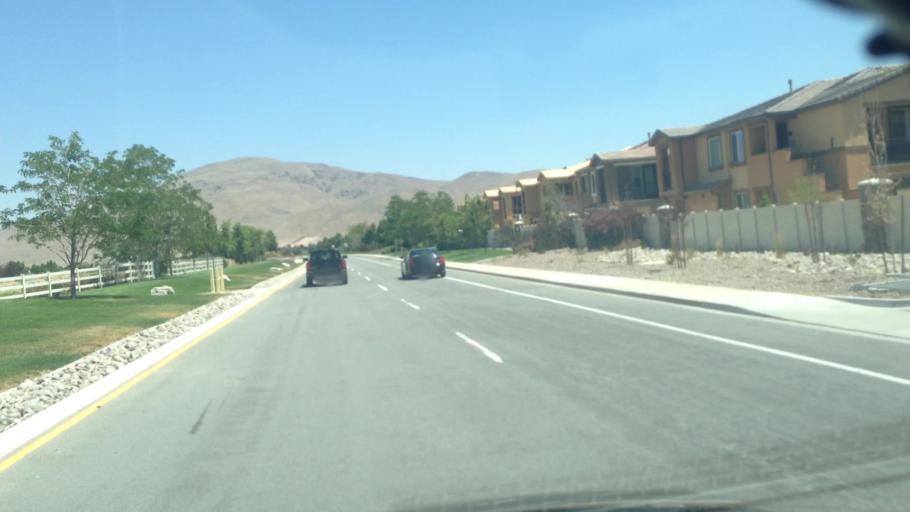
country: US
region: Nevada
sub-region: Washoe County
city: Sparks
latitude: 39.4264
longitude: -119.7320
